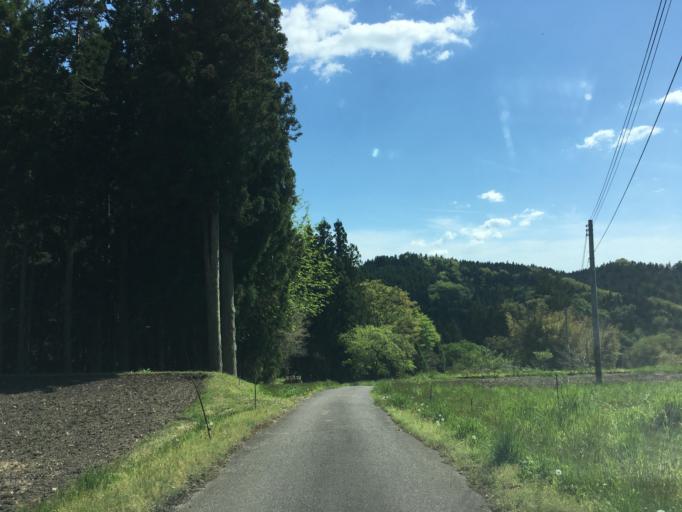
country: JP
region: Fukushima
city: Funehikimachi-funehiki
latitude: 37.3059
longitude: 140.6839
